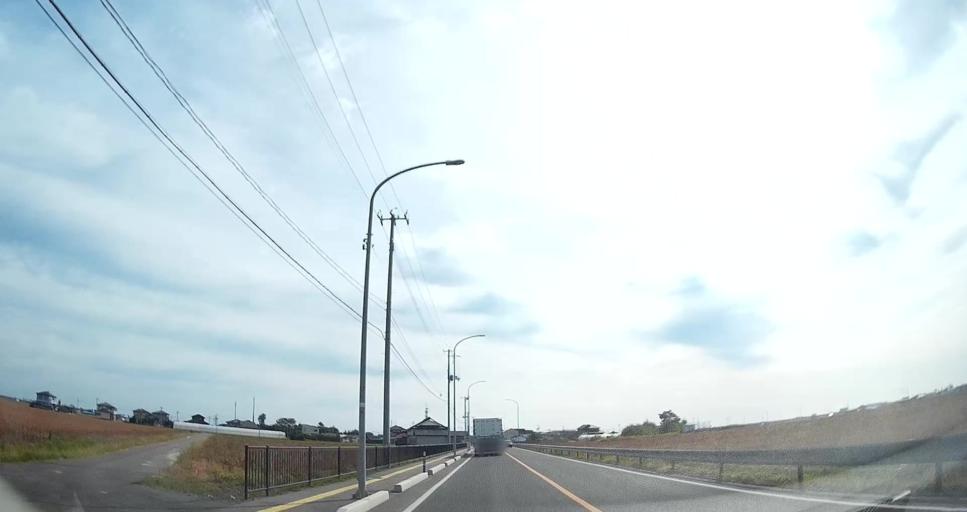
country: JP
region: Miyagi
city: Sendai
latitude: 38.2026
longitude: 140.9458
